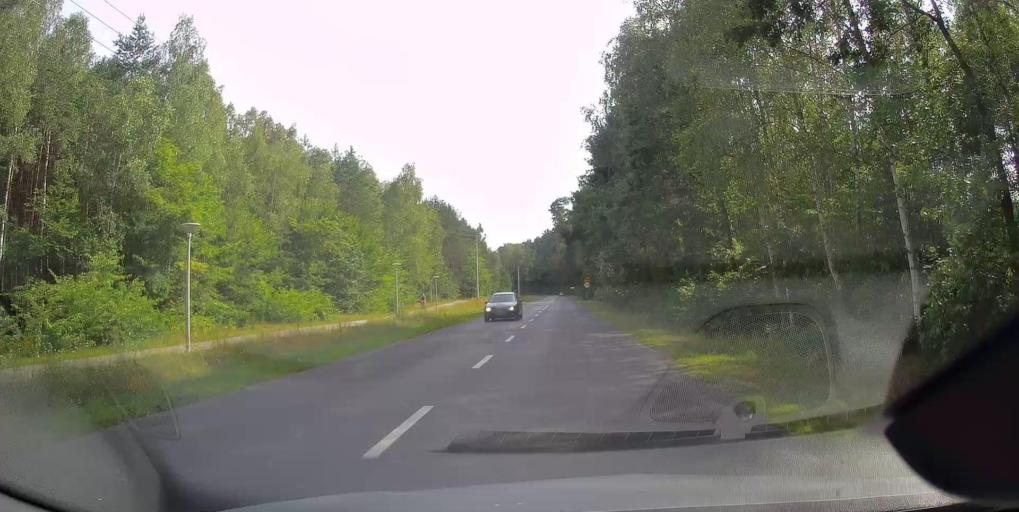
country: PL
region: Lodz Voivodeship
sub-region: Powiat tomaszowski
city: Tomaszow Mazowiecki
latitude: 51.5038
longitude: 19.9961
